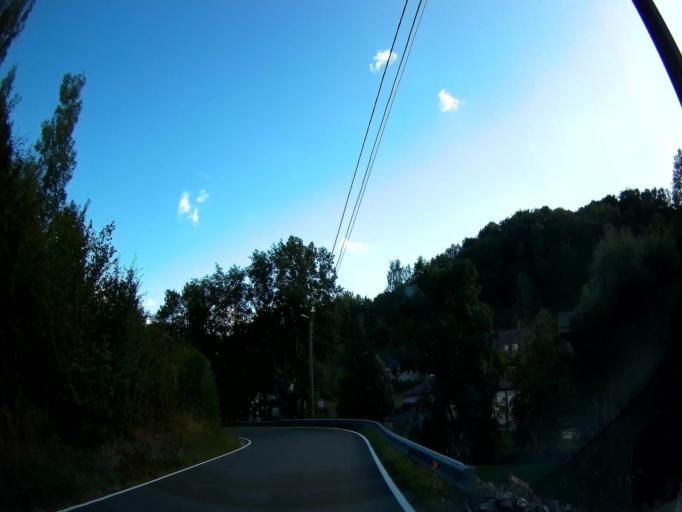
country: BE
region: Wallonia
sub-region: Province de Namur
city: Onhaye
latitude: 50.2966
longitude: 4.7783
